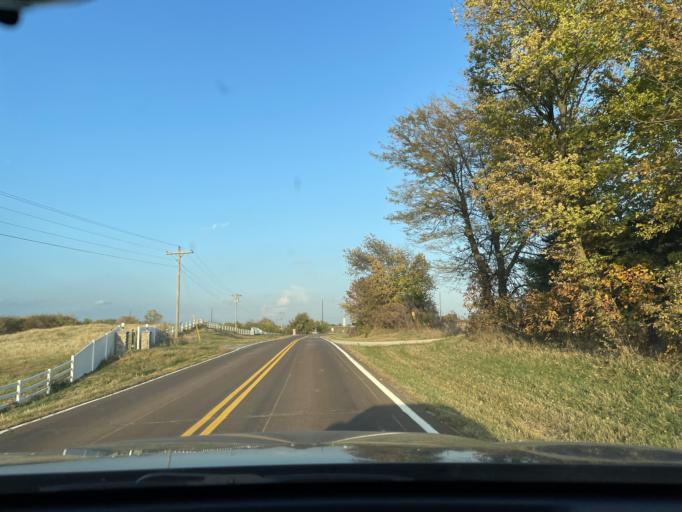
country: US
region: Missouri
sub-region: Andrew County
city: Savannah
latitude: 39.9211
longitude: -94.8650
